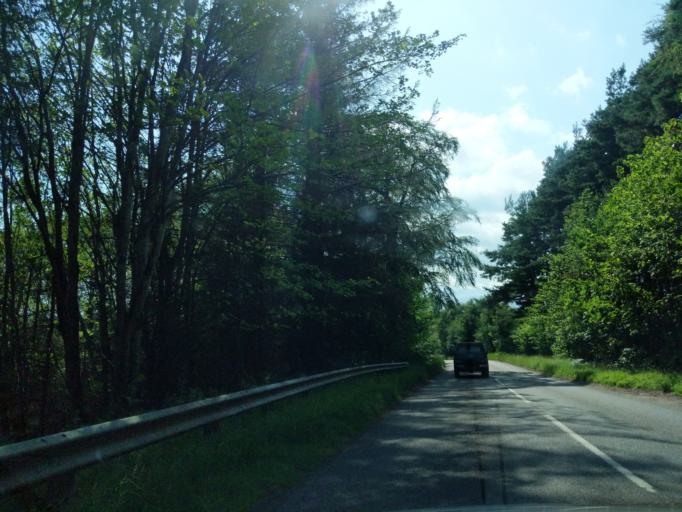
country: GB
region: Scotland
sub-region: Moray
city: Rothes
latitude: 57.4916
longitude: -3.1966
